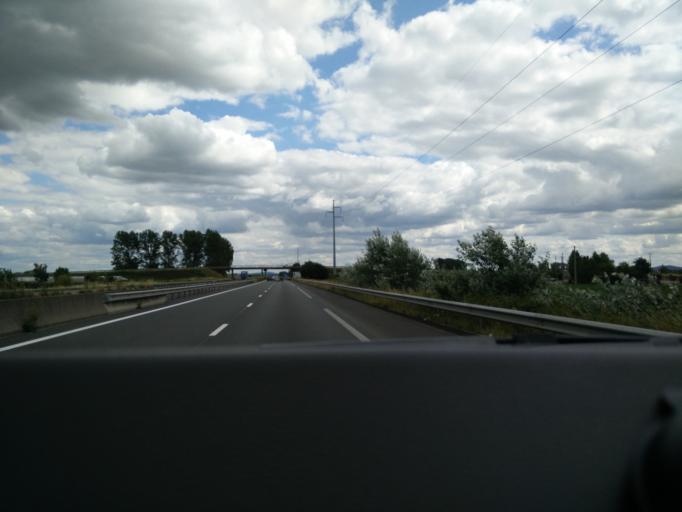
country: FR
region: Nord-Pas-de-Calais
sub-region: Departement du Nord
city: Wormhout
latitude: 50.9043
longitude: 2.4918
